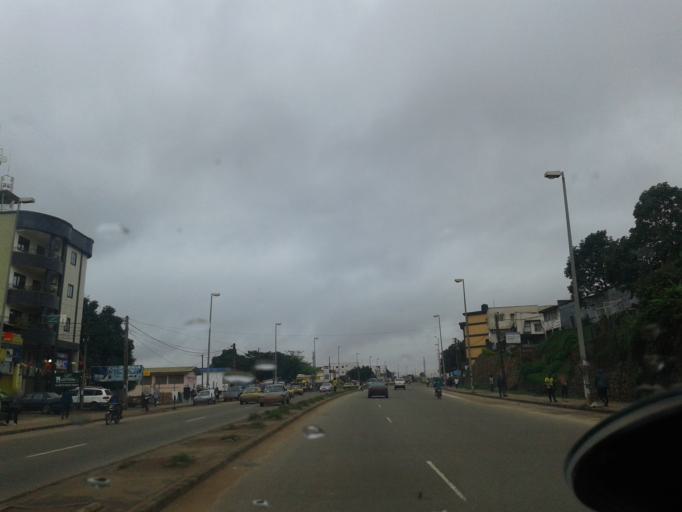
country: CM
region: Centre
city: Yaounde
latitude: 3.8940
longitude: 11.5230
